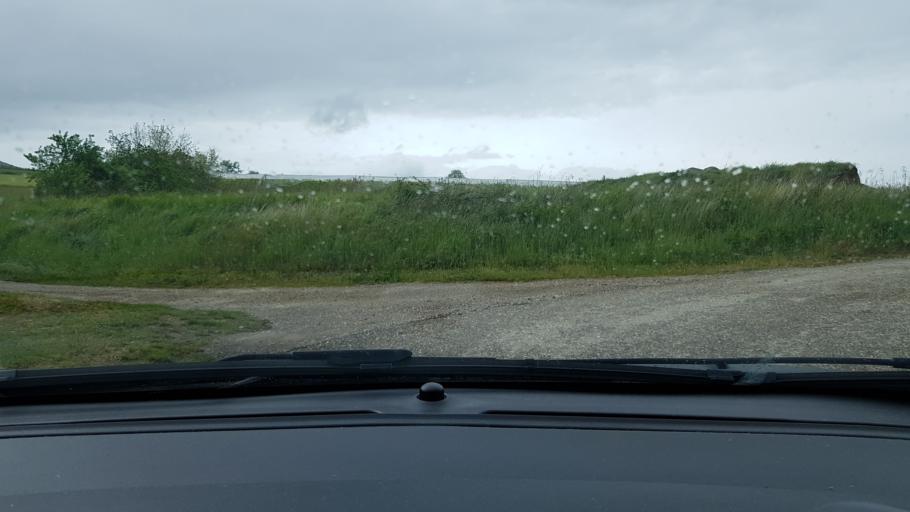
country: FR
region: Rhone-Alpes
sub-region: Departement du Rhone
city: Saint-Maurice-sur-Dargoire
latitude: 45.6061
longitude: 4.6372
